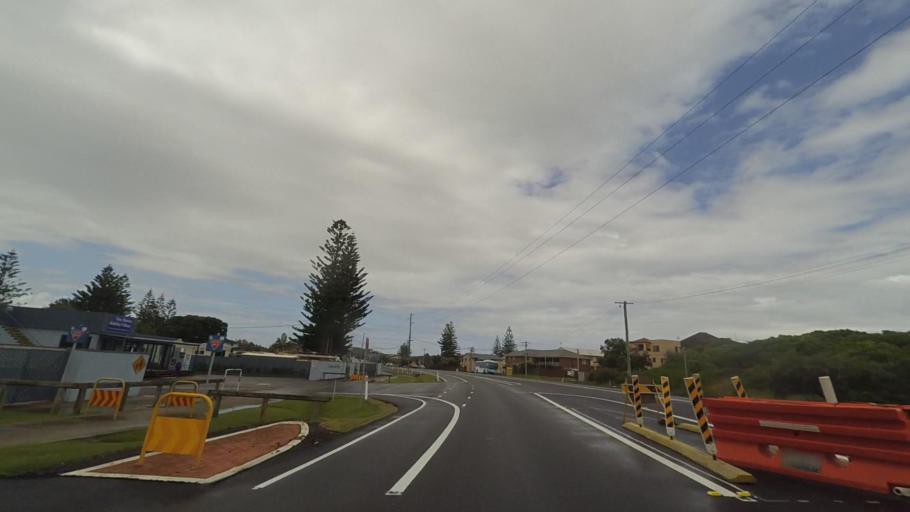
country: AU
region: New South Wales
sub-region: Wyong Shire
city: The Entrance
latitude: -33.3271
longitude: 151.5100
